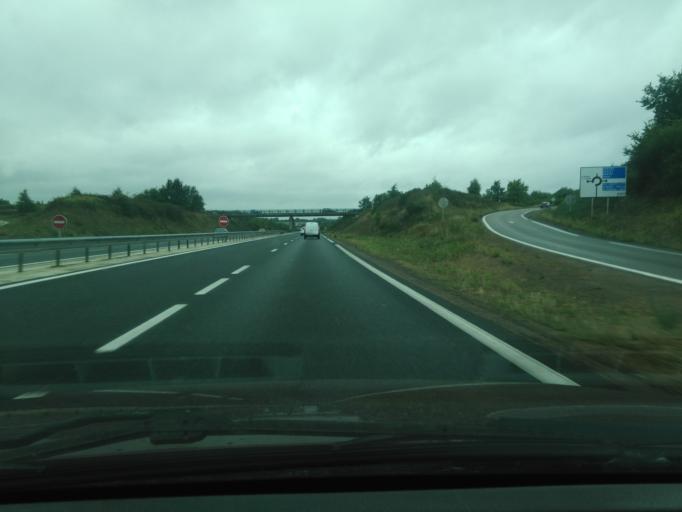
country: FR
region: Pays de la Loire
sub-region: Departement de la Vendee
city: La Ferriere
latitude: 46.6705
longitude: -1.3588
